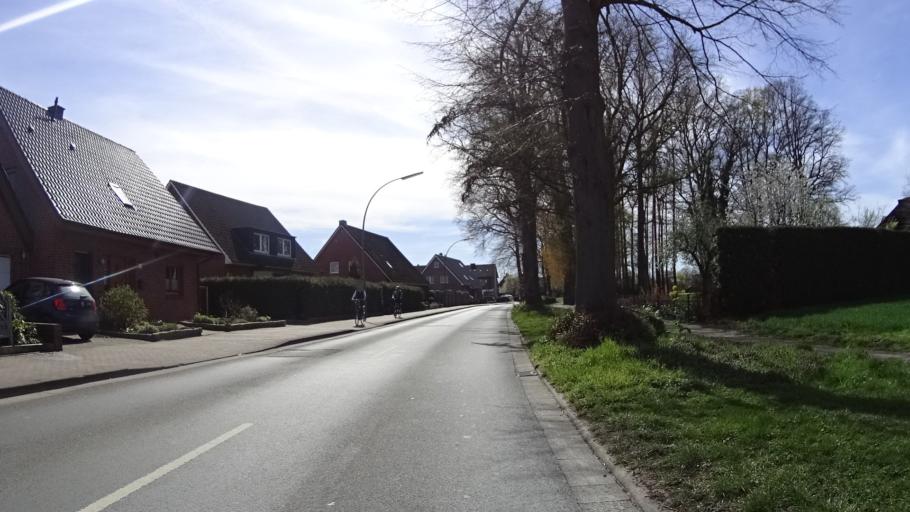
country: DE
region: North Rhine-Westphalia
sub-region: Regierungsbezirk Munster
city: Dreierwalde
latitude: 52.3035
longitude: 7.4718
